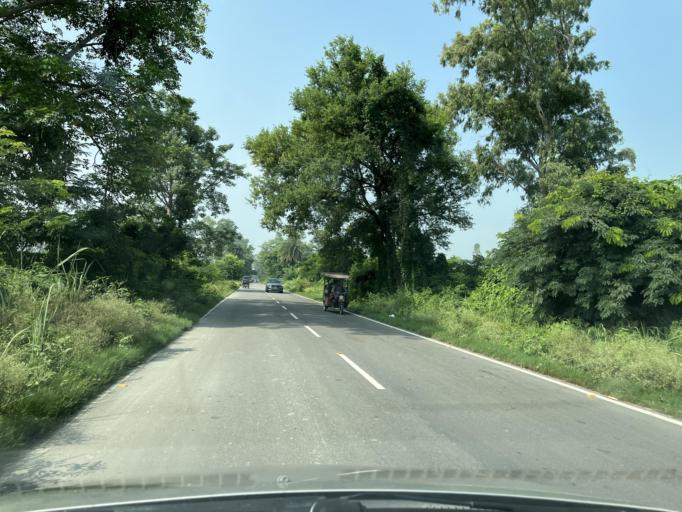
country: IN
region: Uttarakhand
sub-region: Udham Singh Nagar
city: Bazpur
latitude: 29.1798
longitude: 79.1774
